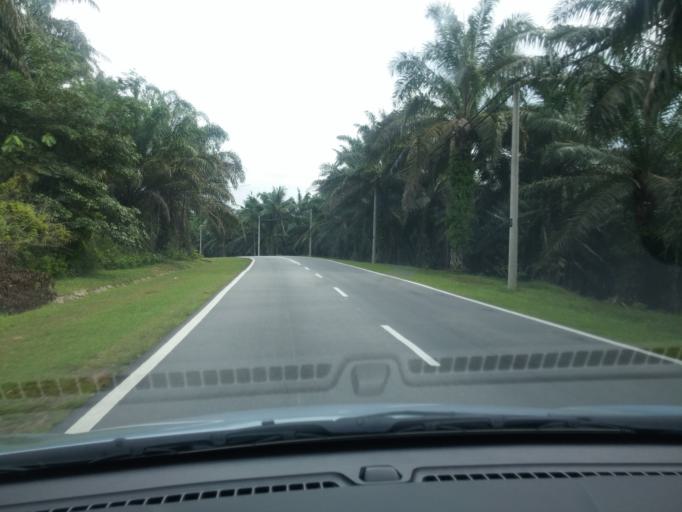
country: MY
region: Pahang
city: Kuantan
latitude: 3.8603
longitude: 103.1646
